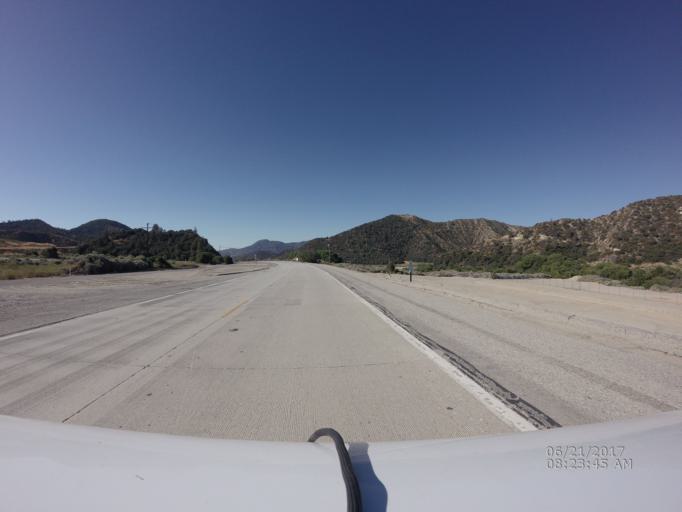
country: US
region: California
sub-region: Kern County
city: Lebec
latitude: 34.7079
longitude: -118.7982
